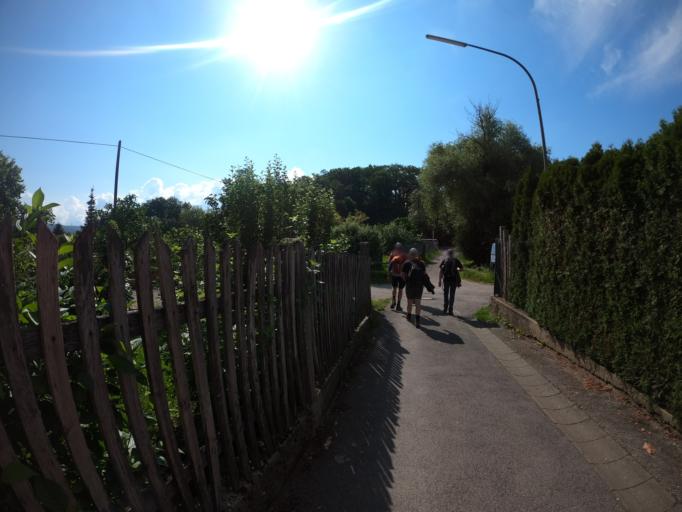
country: DE
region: Bavaria
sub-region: Upper Franconia
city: Strullendorf
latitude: 49.8659
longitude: 10.9973
